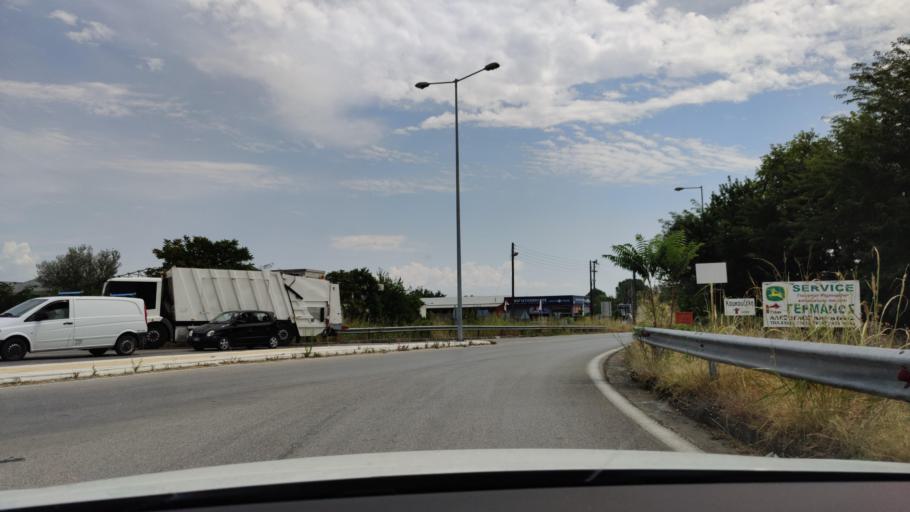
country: GR
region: Central Macedonia
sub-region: Nomos Serron
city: Serres
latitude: 41.0718
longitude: 23.5576
